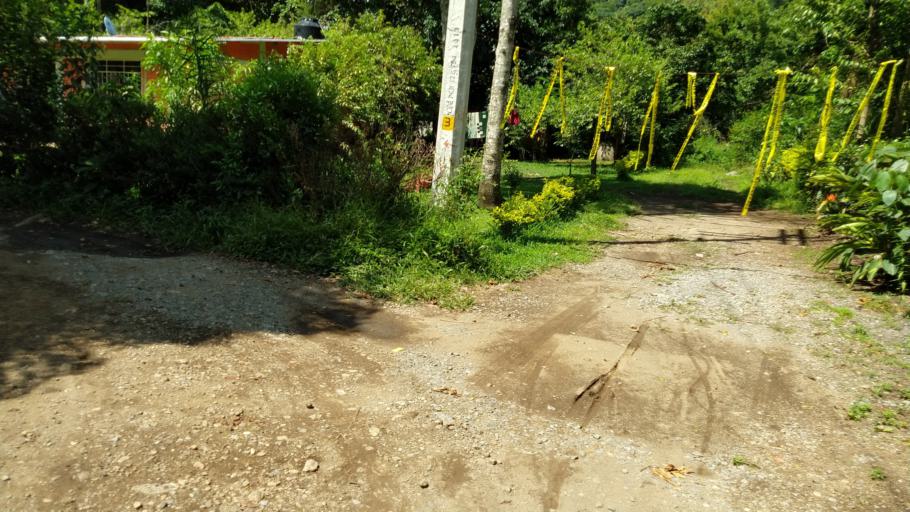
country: MX
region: Veracruz
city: Jalapilla
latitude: 18.8173
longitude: -97.0647
